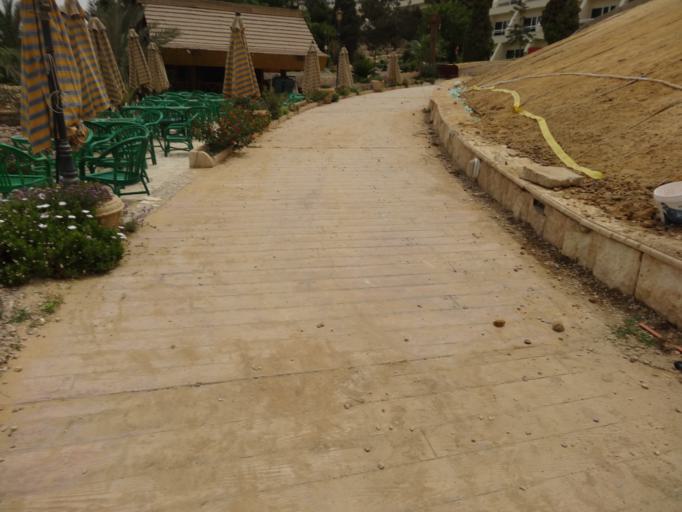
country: EG
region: Muhafazat al Qalyubiyah
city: Al Khankah
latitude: 30.0718
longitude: 31.4352
